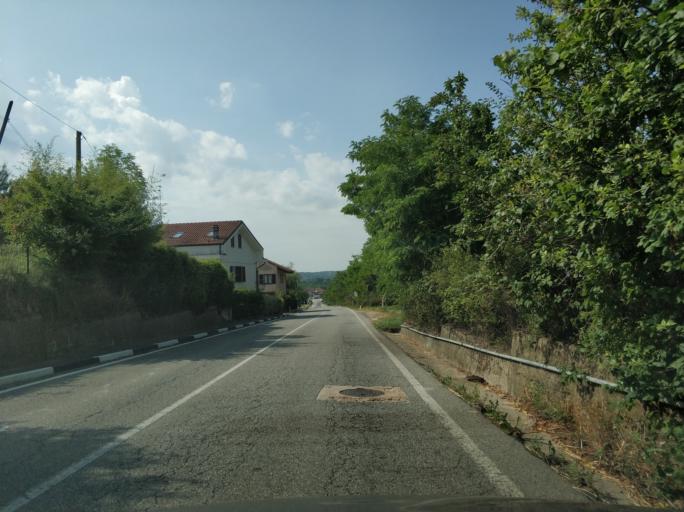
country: IT
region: Piedmont
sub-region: Provincia di Torino
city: Pralormo
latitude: 44.8685
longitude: 7.8962
